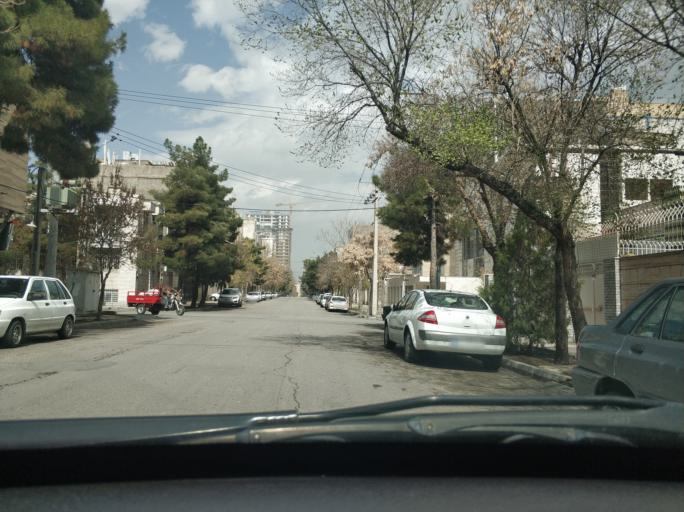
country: IR
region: Razavi Khorasan
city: Mashhad
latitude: 36.2778
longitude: 59.5709
